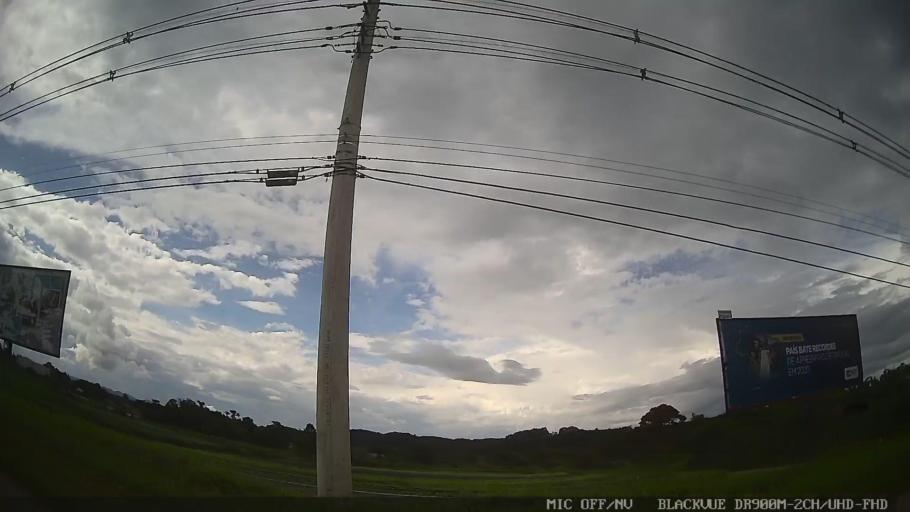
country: BR
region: Sao Paulo
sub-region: Biritiba-Mirim
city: Biritiba Mirim
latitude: -23.5679
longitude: -46.0595
